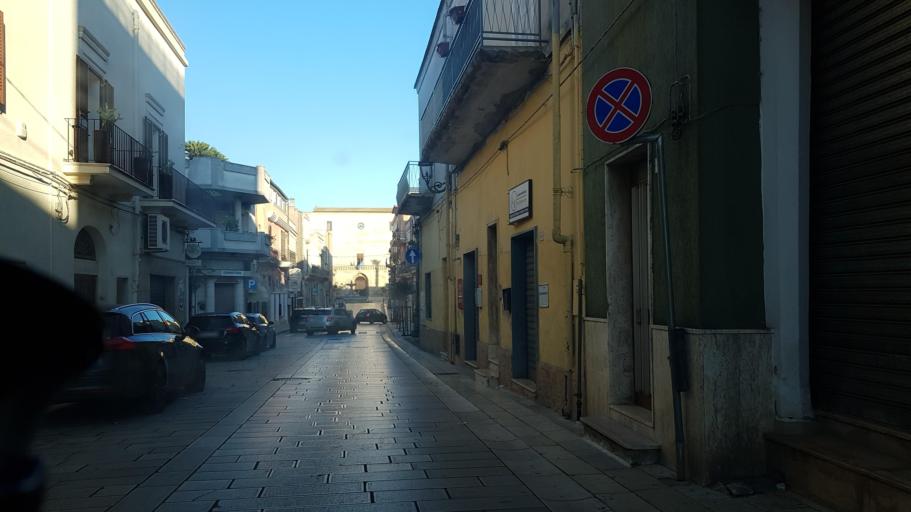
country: IT
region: Apulia
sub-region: Provincia di Brindisi
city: Latiano
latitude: 40.5533
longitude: 17.7160
